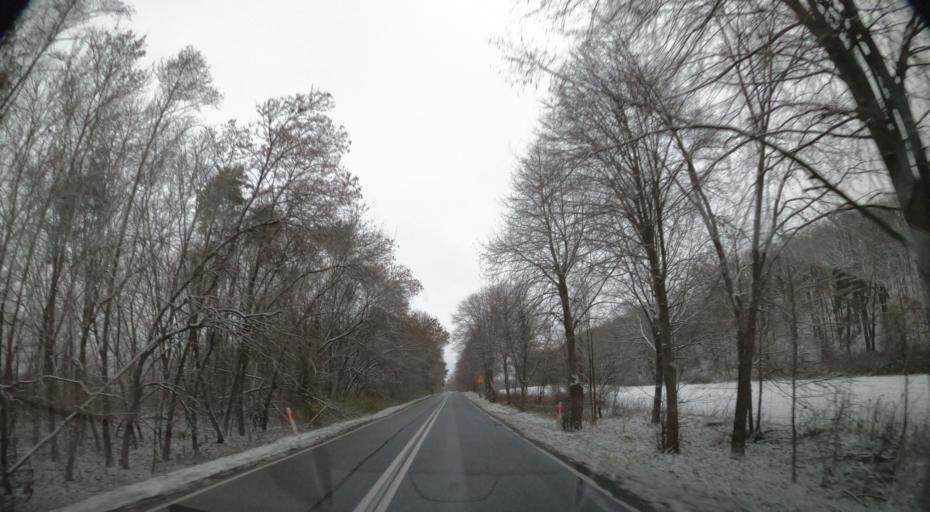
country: PL
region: Masovian Voivodeship
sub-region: Powiat plocki
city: Nowy Duninow
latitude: 52.5777
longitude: 19.5451
